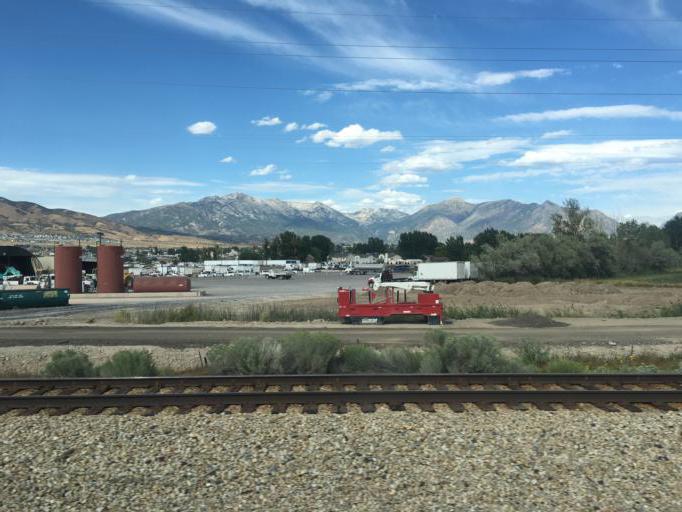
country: US
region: Utah
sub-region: Utah County
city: Lehi
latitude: 40.4075
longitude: -111.8760
